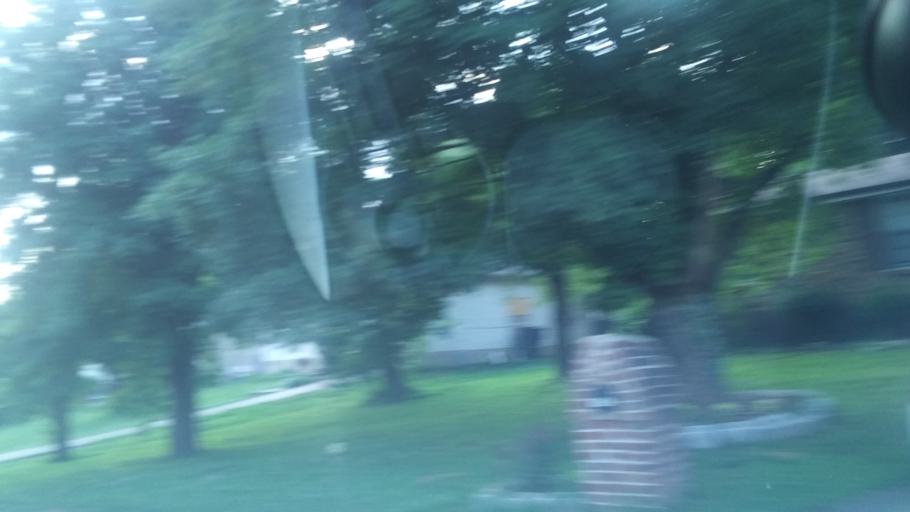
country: US
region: Tennessee
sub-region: Rutherford County
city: La Vergne
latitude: 36.0671
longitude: -86.6666
